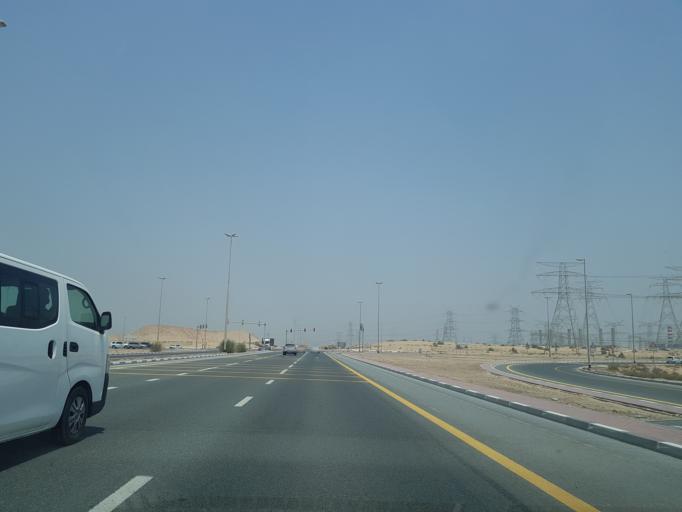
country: AE
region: Ash Shariqah
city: Sharjah
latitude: 25.1379
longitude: 55.4279
